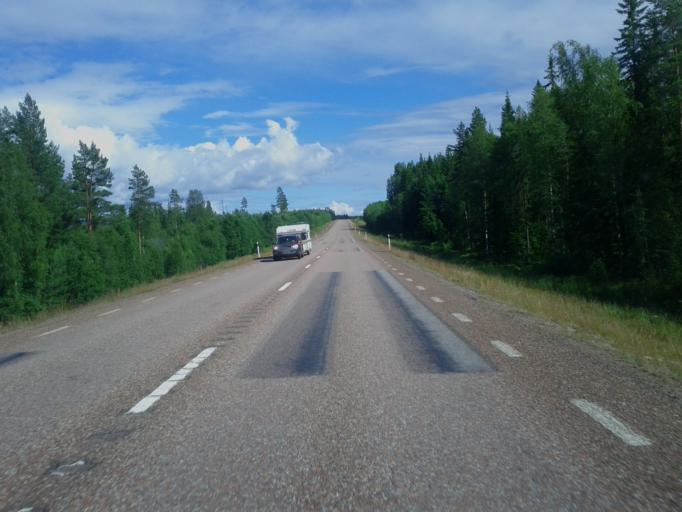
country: SE
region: Dalarna
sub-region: Rattviks Kommun
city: Raettvik
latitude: 60.8416
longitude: 15.2003
